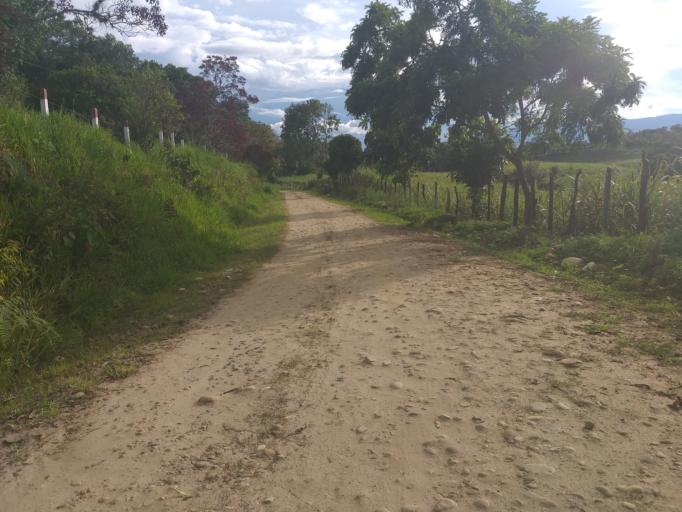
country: CO
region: Boyaca
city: Santana
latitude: 6.0528
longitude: -73.4916
